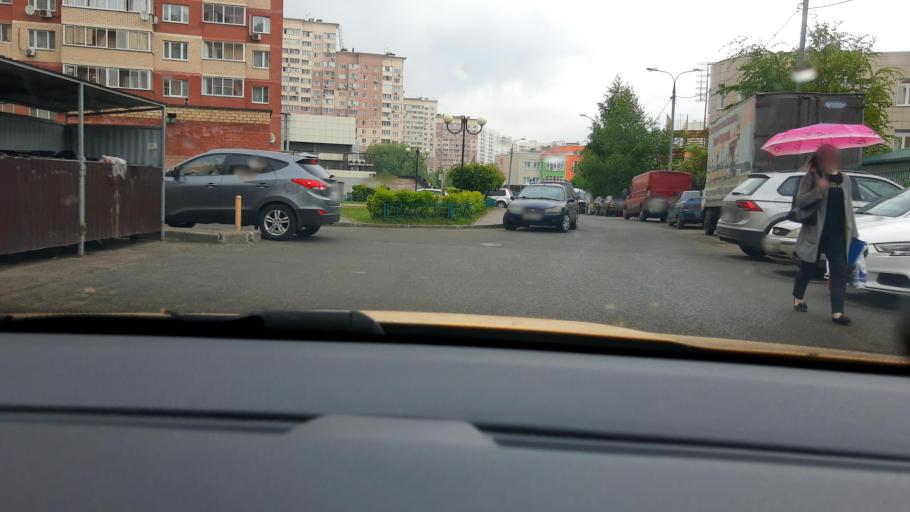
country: RU
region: Moscow
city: Vatutino
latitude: 55.9047
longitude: 37.7000
